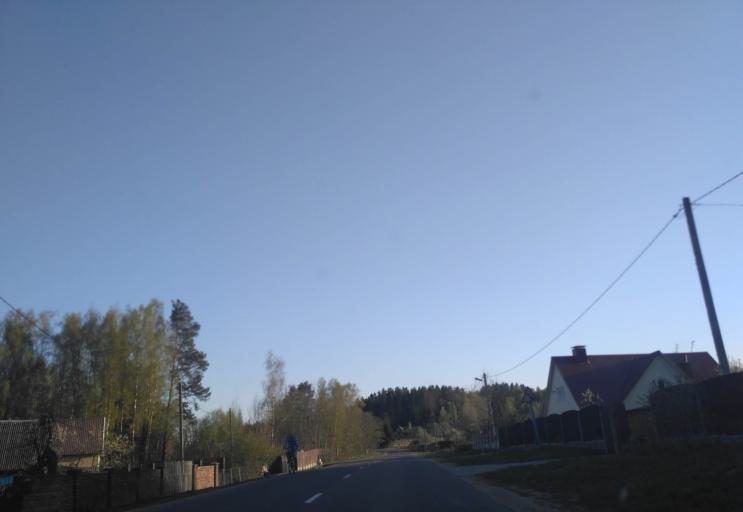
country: BY
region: Minsk
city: Radashkovichy
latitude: 54.1313
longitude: 27.2016
